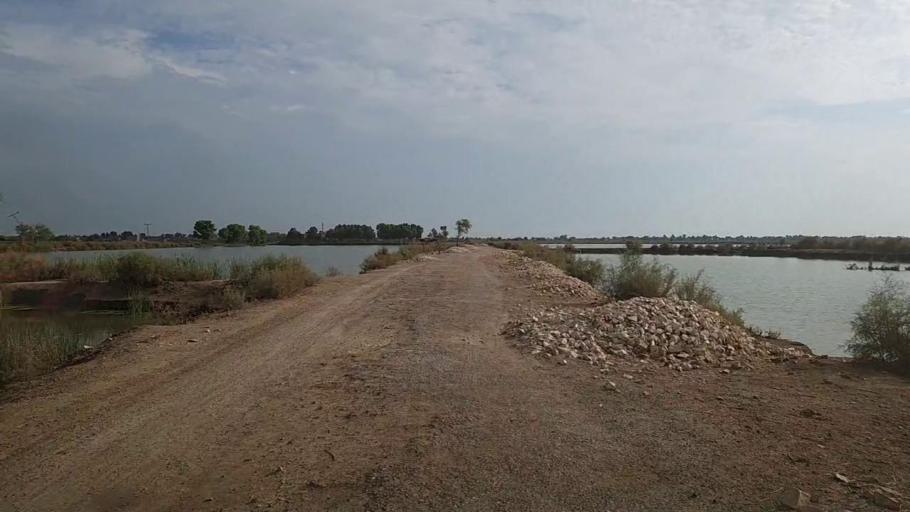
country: PK
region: Sindh
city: Thul
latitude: 28.2748
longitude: 68.8546
